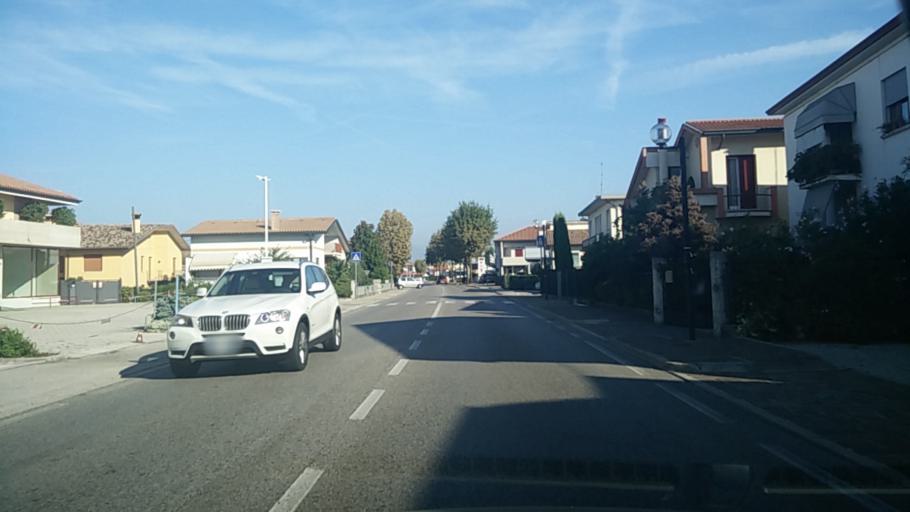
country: IT
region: Veneto
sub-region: Provincia di Treviso
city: Resana
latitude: 45.6360
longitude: 11.9549
